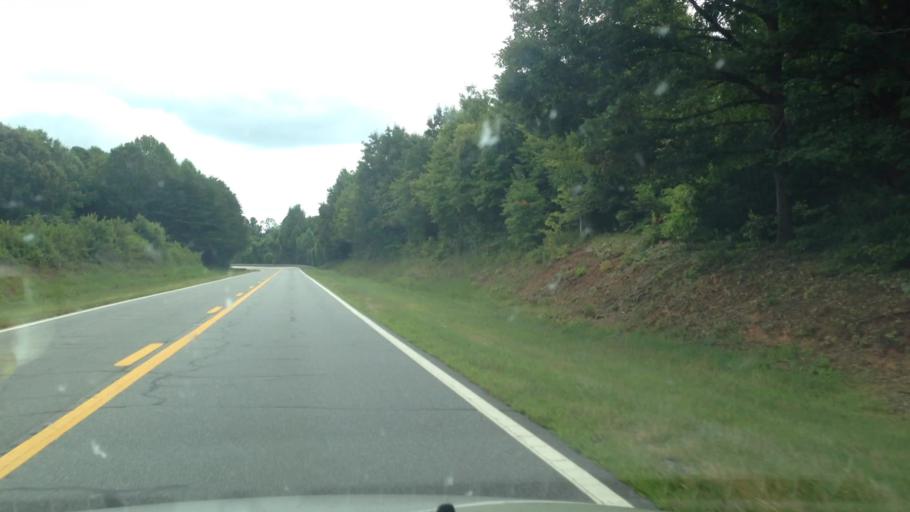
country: US
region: North Carolina
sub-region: Rockingham County
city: Wentworth
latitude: 36.3892
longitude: -79.8142
